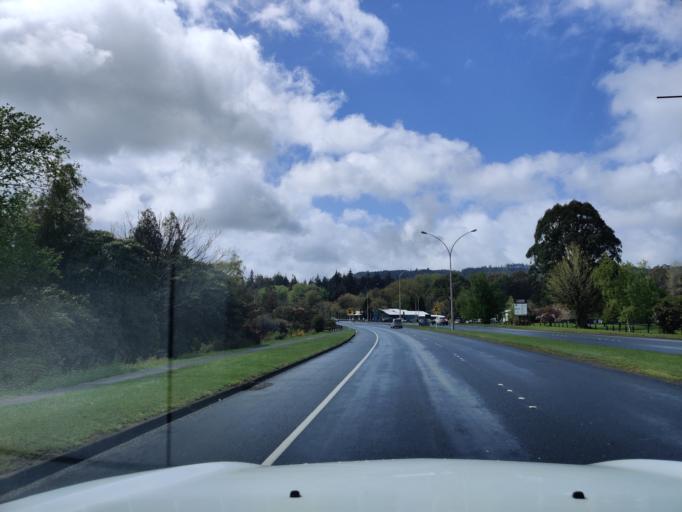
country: NZ
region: Bay of Plenty
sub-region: Rotorua District
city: Rotorua
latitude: -38.1494
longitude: 176.2640
